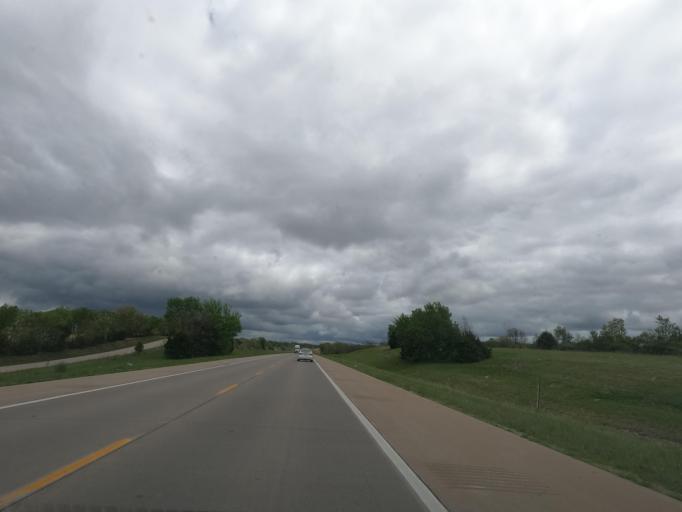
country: US
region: Kansas
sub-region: Wilson County
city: Neodesha
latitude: 37.3550
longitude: -95.6508
